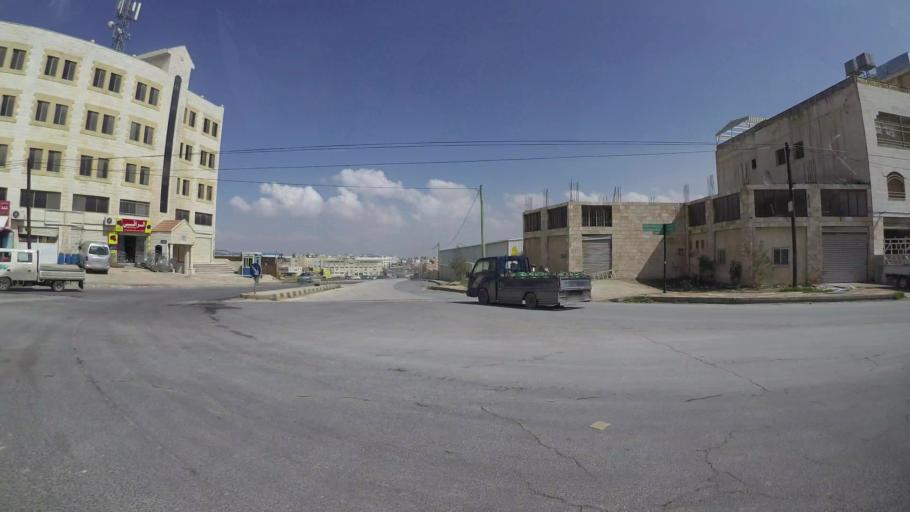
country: JO
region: Zarqa
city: Russeifa
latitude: 31.9907
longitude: 36.0084
